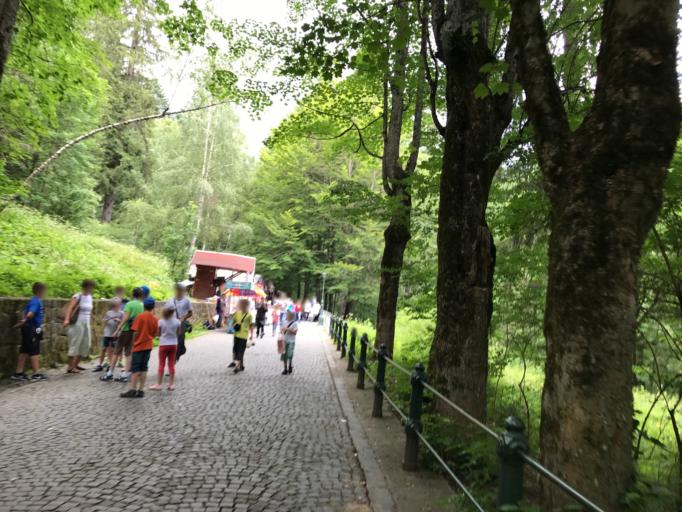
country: RO
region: Prahova
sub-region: Oras Sinaia
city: Sinaia
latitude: 45.3573
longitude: 25.5462
